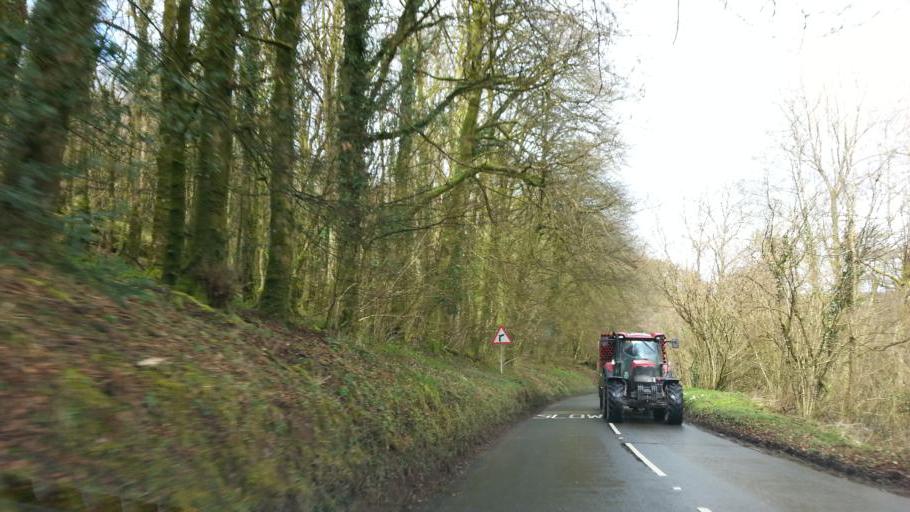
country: GB
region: England
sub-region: Devon
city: Combe Martin
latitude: 51.1486
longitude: -3.9972
